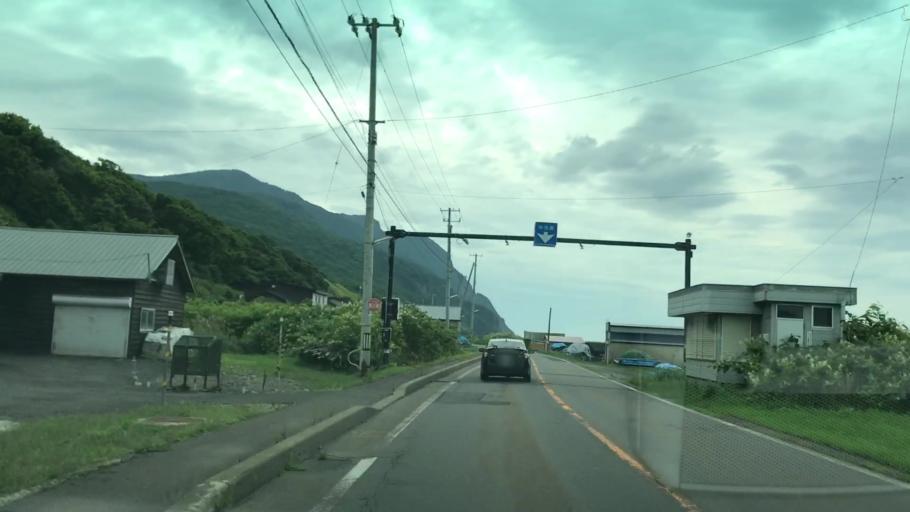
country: JP
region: Hokkaido
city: Iwanai
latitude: 42.9665
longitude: 140.4717
